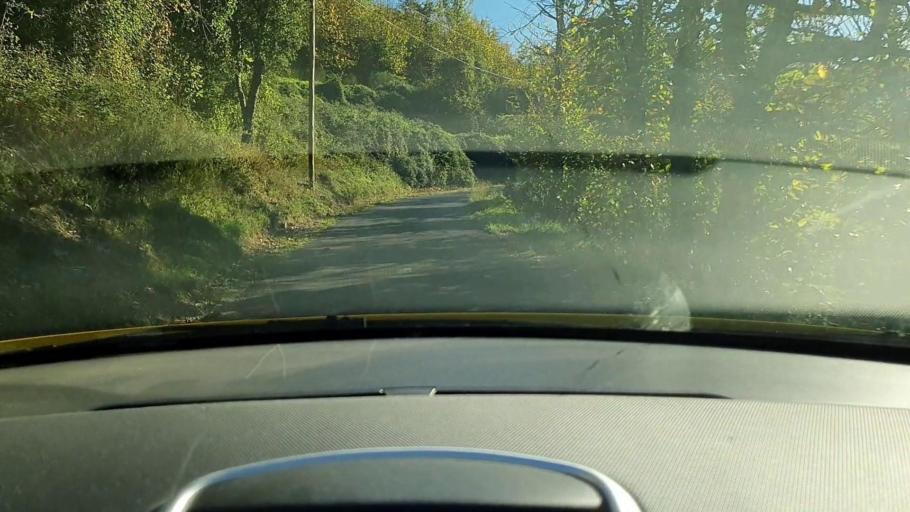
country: FR
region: Languedoc-Roussillon
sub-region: Departement du Gard
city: Sumene
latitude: 44.0270
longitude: 3.7612
